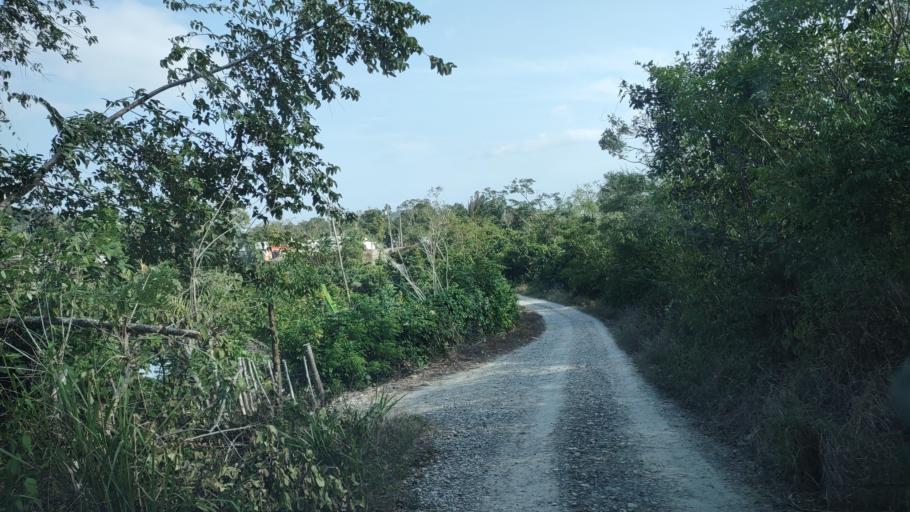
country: MX
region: Veracruz
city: Papantla de Olarte
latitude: 20.4589
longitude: -97.3949
